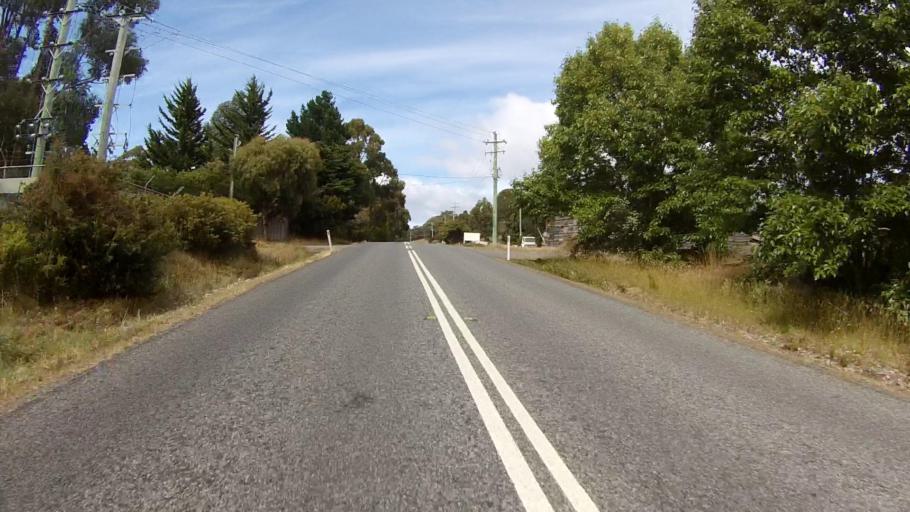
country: AU
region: Tasmania
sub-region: Kingborough
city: Kettering
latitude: -43.1379
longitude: 147.2457
